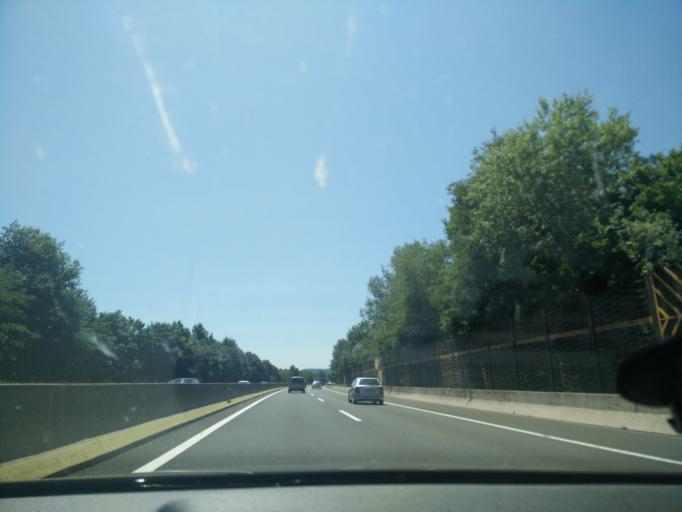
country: AT
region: Styria
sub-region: Politischer Bezirk Hartberg-Fuerstenfeld
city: Sebersdorf
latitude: 47.2210
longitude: 15.9953
